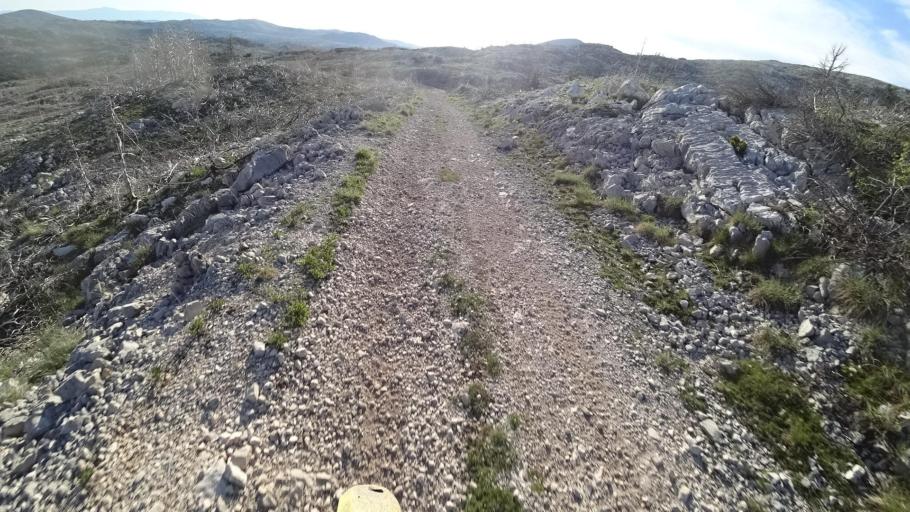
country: BA
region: Federation of Bosnia and Herzegovina
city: Kocerin
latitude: 43.5779
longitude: 17.5405
